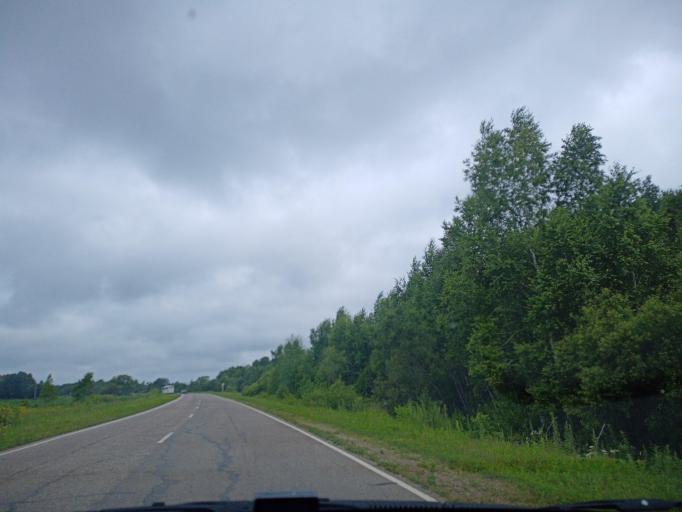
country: RU
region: Primorskiy
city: Novopokrovka
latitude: 45.9693
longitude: 134.2443
